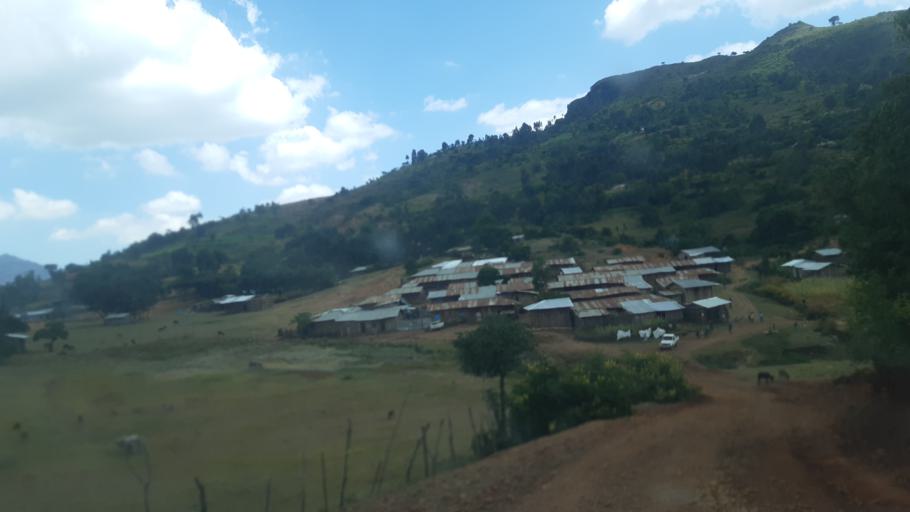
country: ET
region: Amhara
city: Dabat
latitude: 13.3382
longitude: 37.4212
